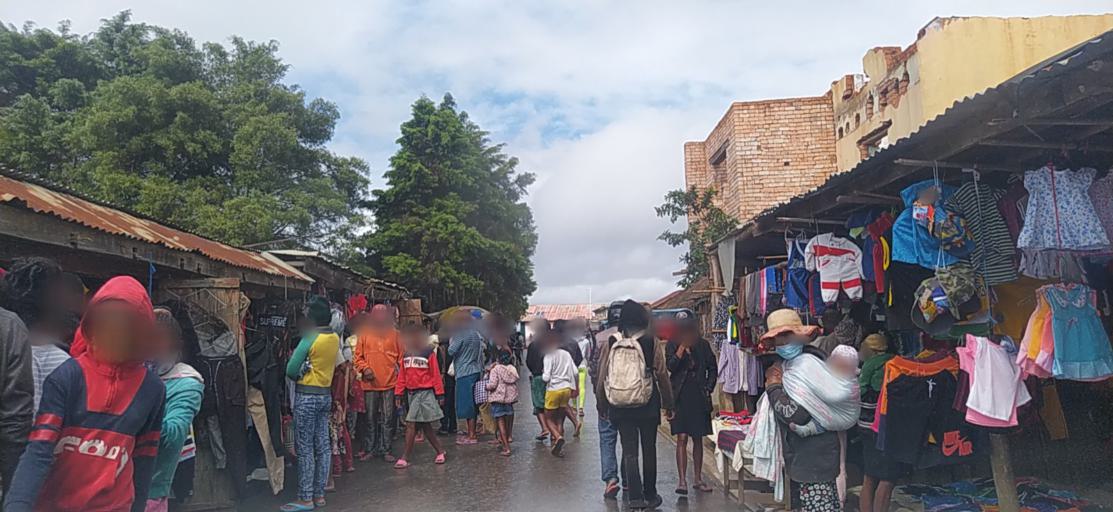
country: MG
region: Analamanga
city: Anjozorobe
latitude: -18.4438
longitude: 48.2633
